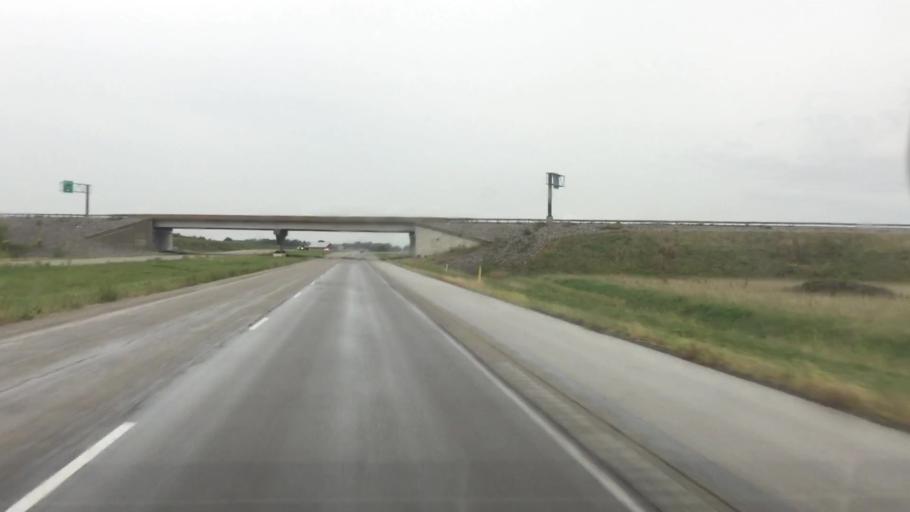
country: US
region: Indiana
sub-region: Allen County
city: Woodburn
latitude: 41.1149
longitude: -84.9209
